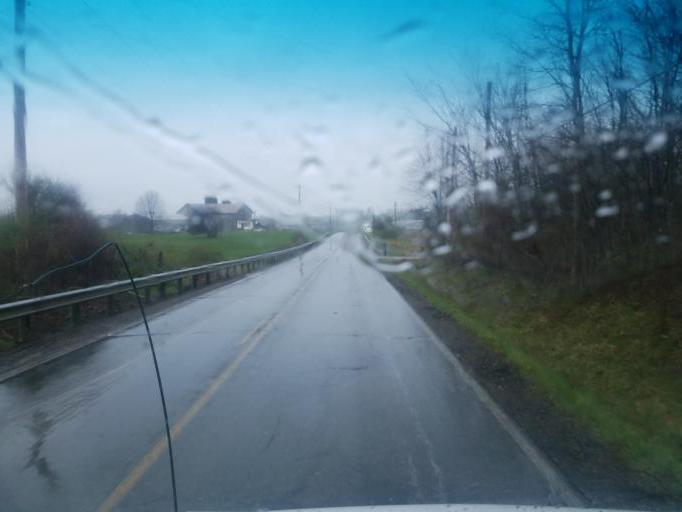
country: US
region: Ohio
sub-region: Wayne County
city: Apple Creek
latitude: 40.7069
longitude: -81.8894
